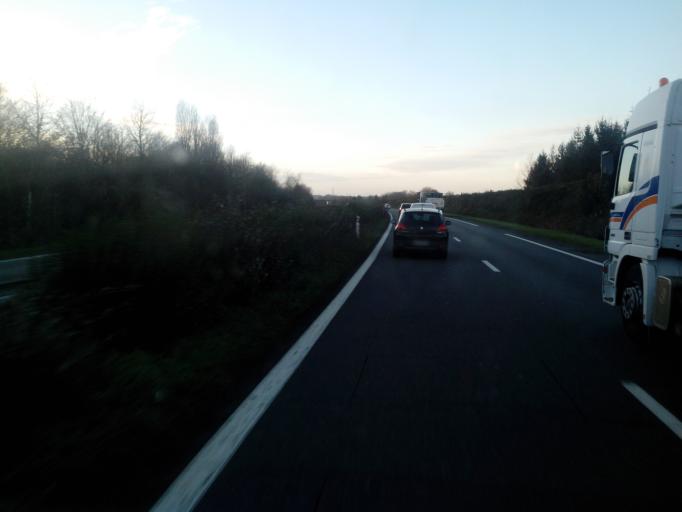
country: FR
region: Pays de la Loire
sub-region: Departement de la Loire-Atlantique
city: La Chapelle-Heulin
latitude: 47.1591
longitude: -1.3435
